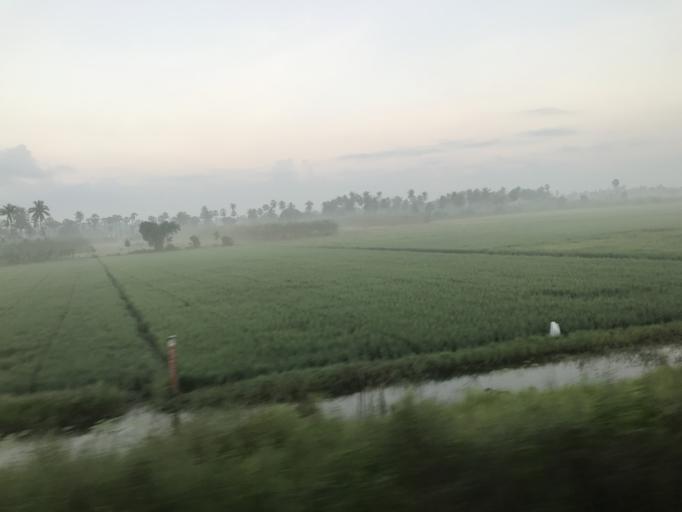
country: IN
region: Andhra Pradesh
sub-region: Guntur
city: Ponnur
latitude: 16.0820
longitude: 80.5638
